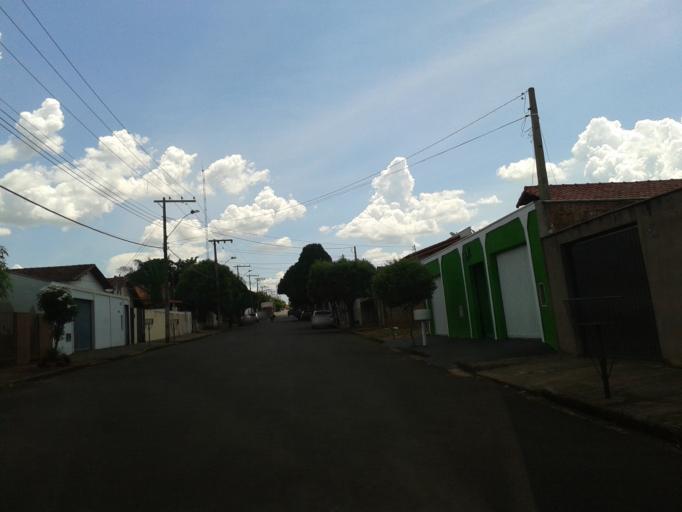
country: BR
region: Minas Gerais
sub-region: Ituiutaba
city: Ituiutaba
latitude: -18.9819
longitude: -49.4513
